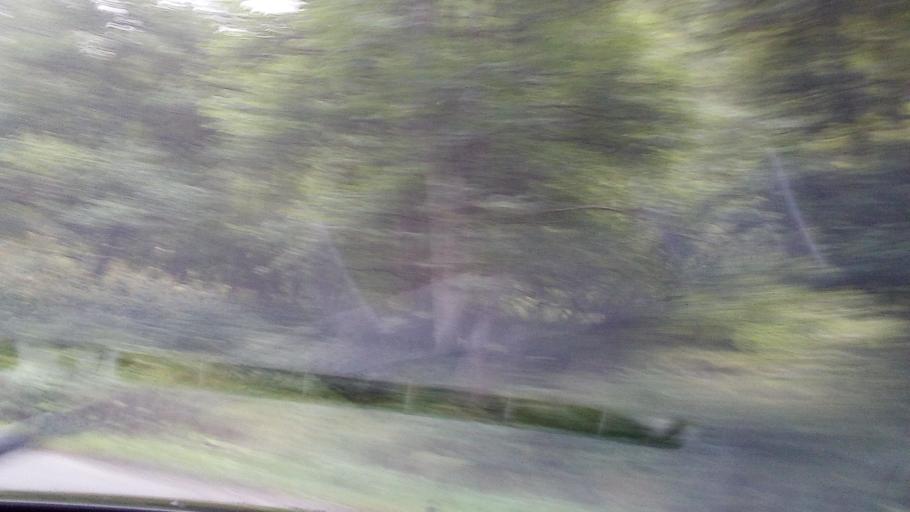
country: FR
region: Midi-Pyrenees
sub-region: Departement des Hautes-Pyrenees
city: Cauterets
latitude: 42.9504
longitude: -0.2032
